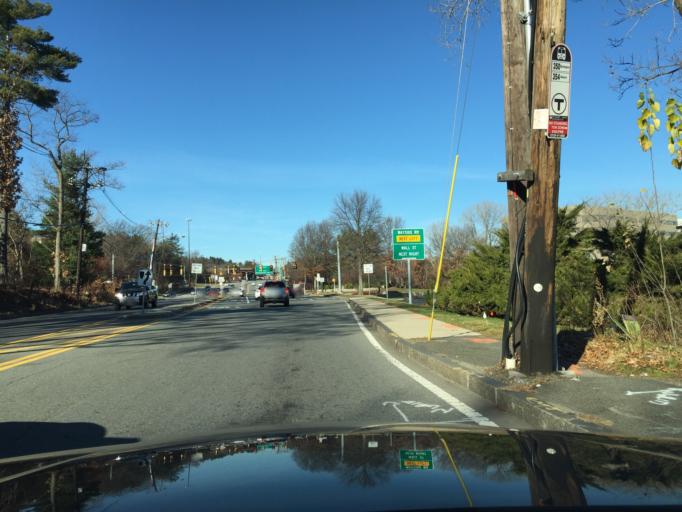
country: US
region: Massachusetts
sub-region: Middlesex County
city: Burlington
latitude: 42.4847
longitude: -71.1895
